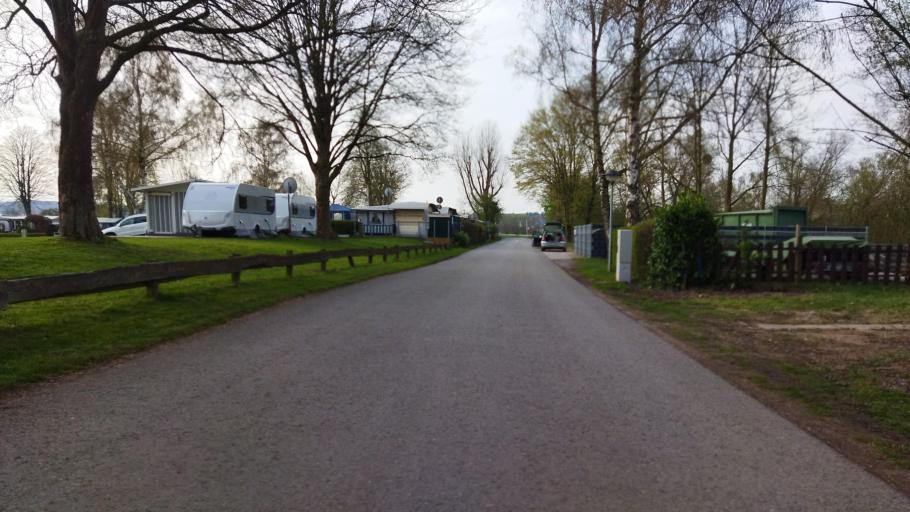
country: DE
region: Lower Saxony
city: Rinteln
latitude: 52.1845
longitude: 9.0453
